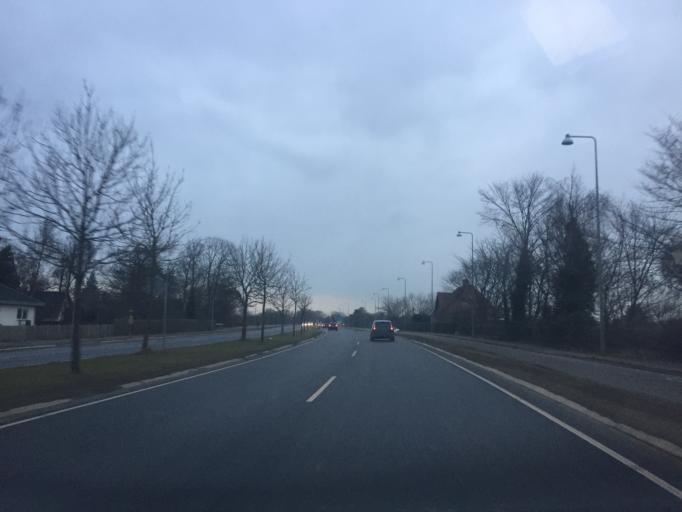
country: DK
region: Zealand
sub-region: Solrod Kommune
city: Solrod Strand
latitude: 55.5077
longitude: 12.2020
